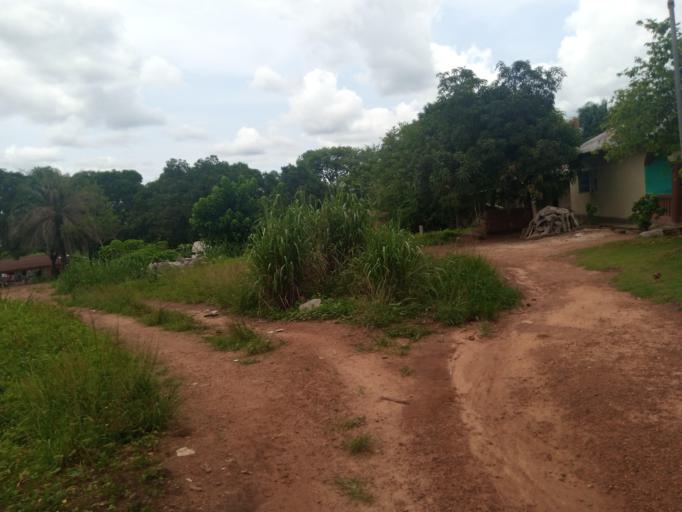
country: SL
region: Southern Province
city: Bo
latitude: 7.9578
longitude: -11.7153
